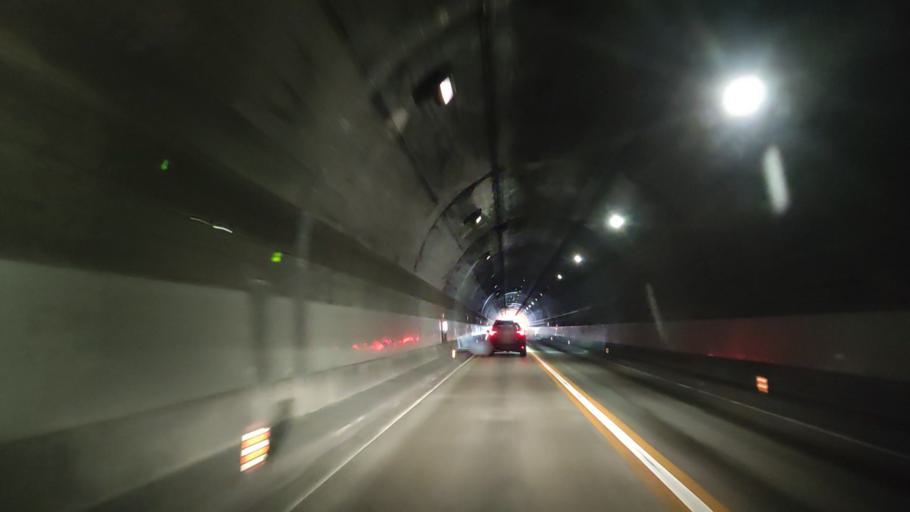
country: JP
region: Tokushima
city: Kamojimacho-jogejima
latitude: 34.1673
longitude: 134.3319
